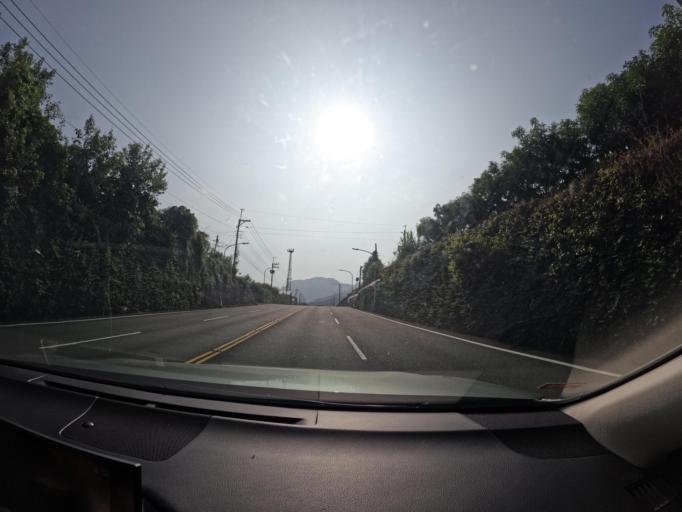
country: TW
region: Taiwan
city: Yujing
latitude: 23.0719
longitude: 120.5072
